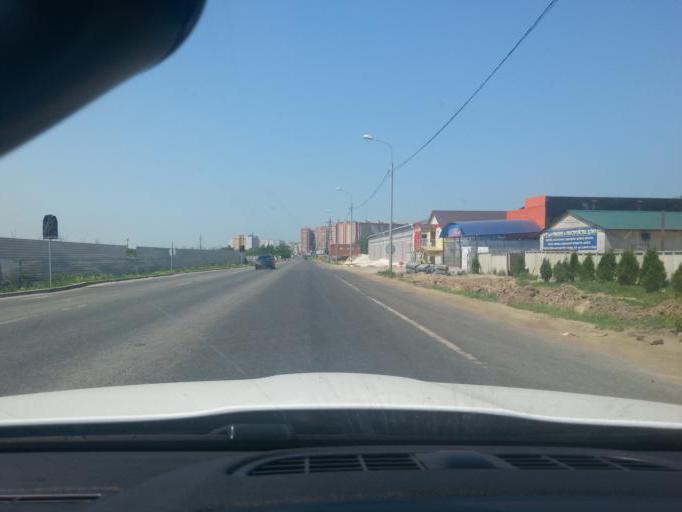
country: RU
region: Moskovskaya
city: Zheleznodorozhnyy
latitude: 55.7258
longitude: 37.9918
